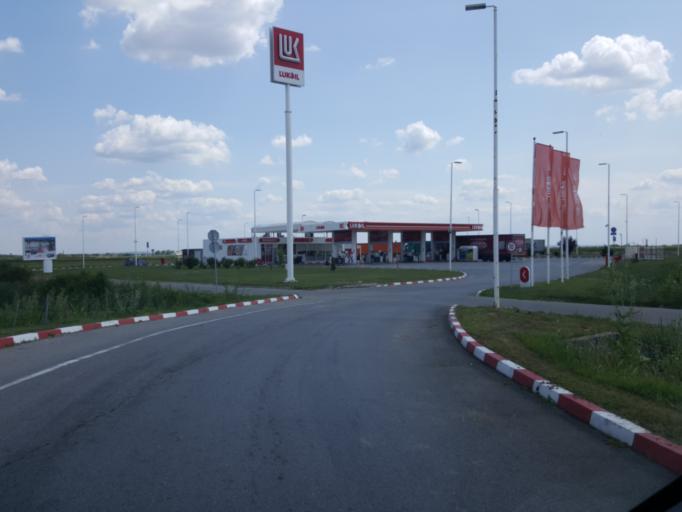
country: RS
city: Ugrinovci
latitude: 44.8505
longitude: 20.1863
